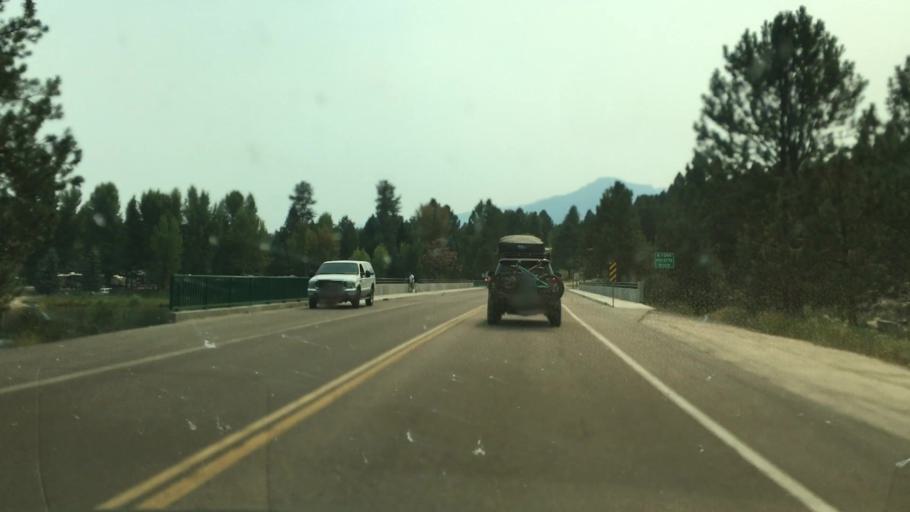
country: US
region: Idaho
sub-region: Valley County
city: Cascade
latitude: 44.5250
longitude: -116.0439
